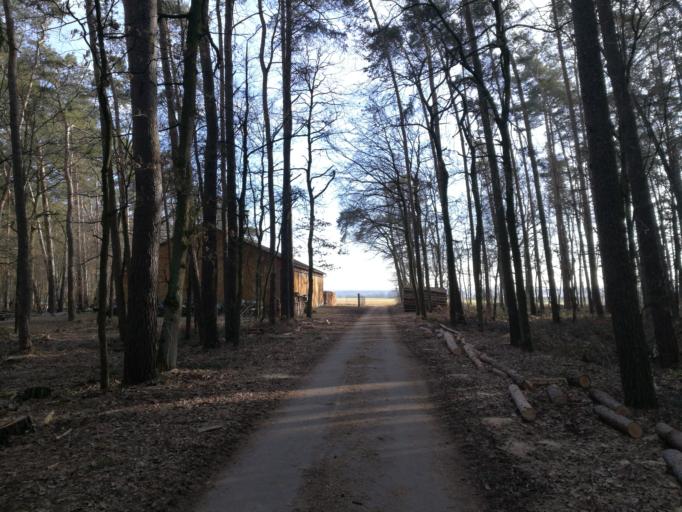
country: DE
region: Bavaria
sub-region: Regierungsbezirk Mittelfranken
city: Veitsbronn
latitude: 49.5251
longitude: 10.8845
